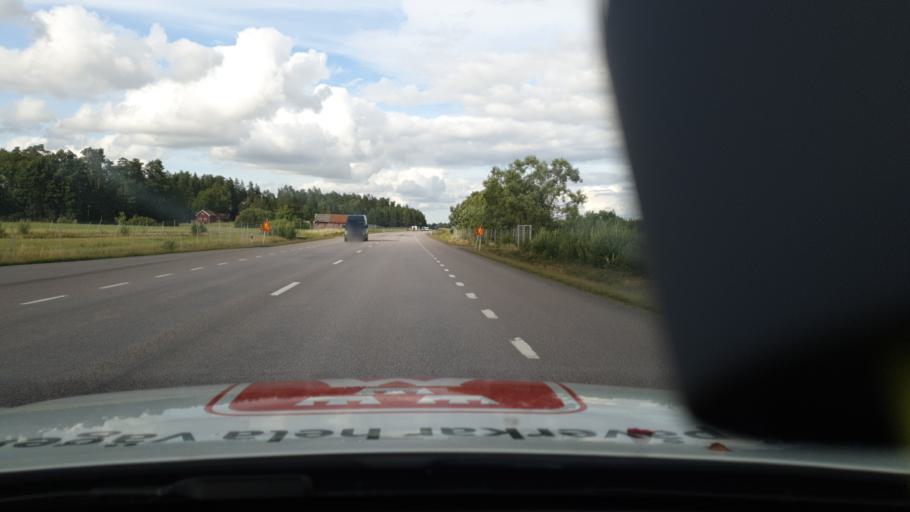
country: SE
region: Vaestra Goetaland
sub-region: Grastorps Kommun
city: Graestorp
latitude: 58.3048
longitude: 12.5443
